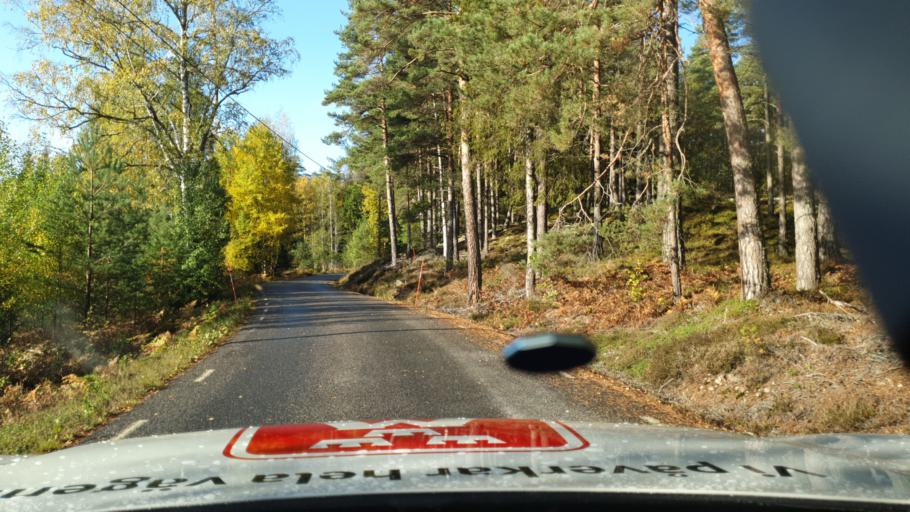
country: SE
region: Kalmar
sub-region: Vasterviks Kommun
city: Forserum
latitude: 57.9962
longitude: 16.5461
